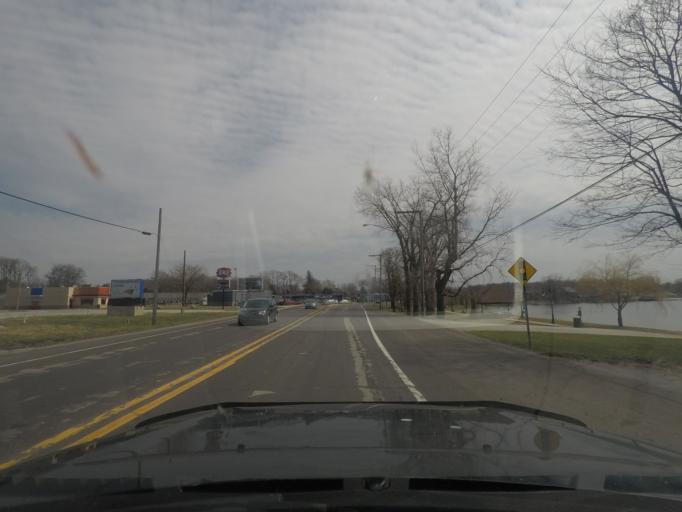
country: US
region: Indiana
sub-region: LaPorte County
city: LaPorte
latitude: 41.6329
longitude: -86.7411
